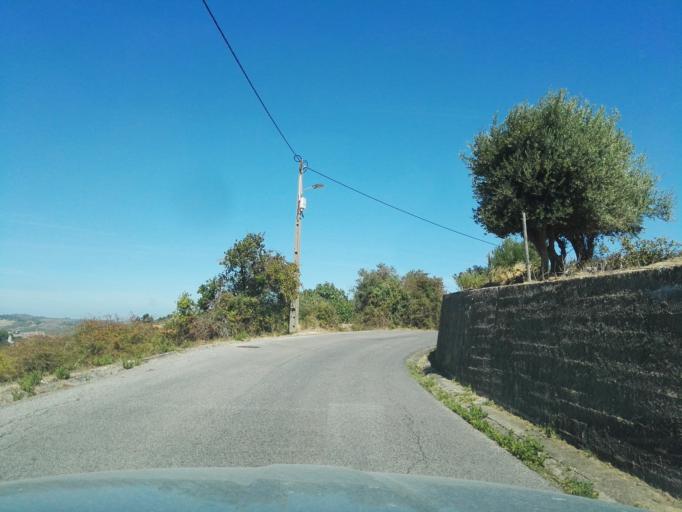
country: PT
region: Lisbon
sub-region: Vila Franca de Xira
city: Sao Joao dos Montes
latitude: 38.9614
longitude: -9.0248
